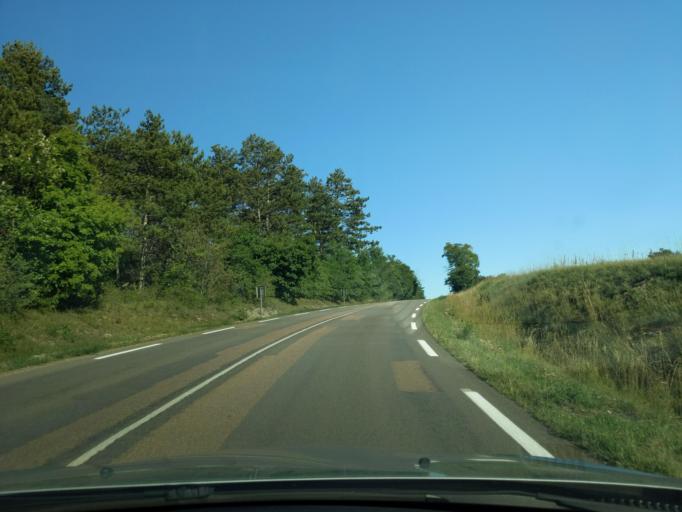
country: FR
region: Bourgogne
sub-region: Departement de la Cote-d'Or
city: Is-sur-Tille
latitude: 47.5054
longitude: 5.0783
